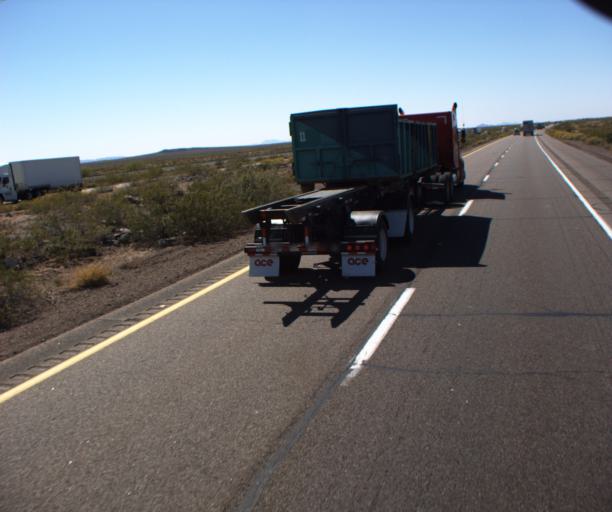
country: US
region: Arizona
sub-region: Maricopa County
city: Gila Bend
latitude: 32.8631
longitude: -113.1695
